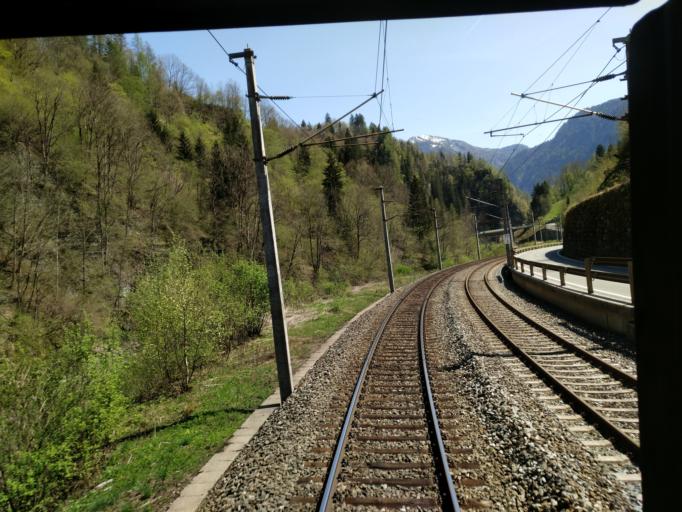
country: AT
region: Salzburg
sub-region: Politischer Bezirk Zell am See
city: Lend
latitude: 47.3068
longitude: 13.0296
